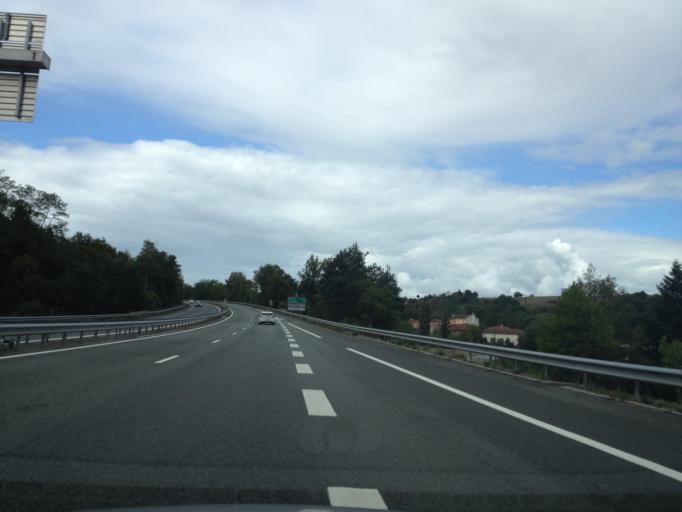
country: FR
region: Rhone-Alpes
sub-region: Departement de la Loire
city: Perreux
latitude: 45.9704
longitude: 4.1329
